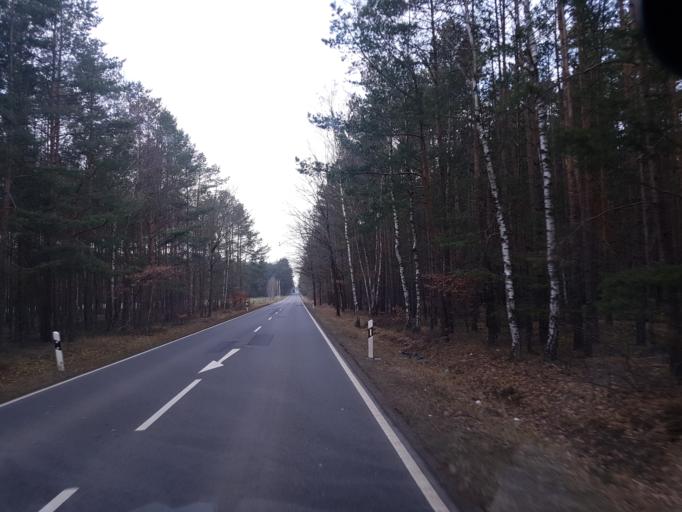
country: DE
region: Brandenburg
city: Finsterwalde
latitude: 51.6033
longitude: 13.7751
